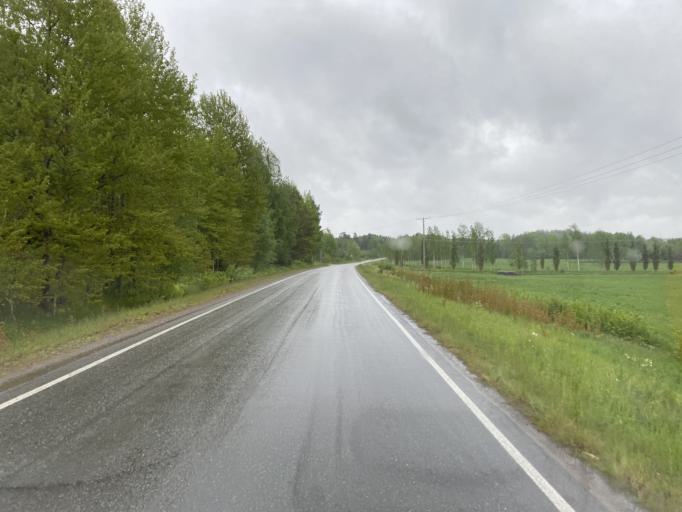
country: FI
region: Pirkanmaa
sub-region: Etelae-Pirkanmaa
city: Urjala
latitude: 61.0426
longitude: 23.4268
